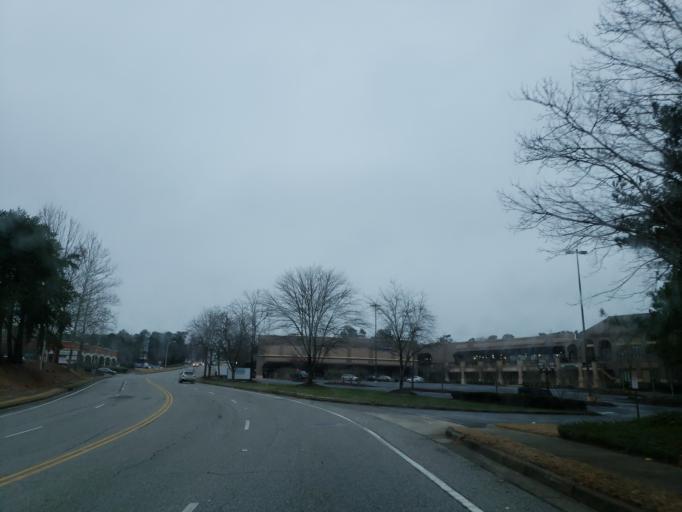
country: US
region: Georgia
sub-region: Fulton County
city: Roswell
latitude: 34.0173
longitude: -84.3188
